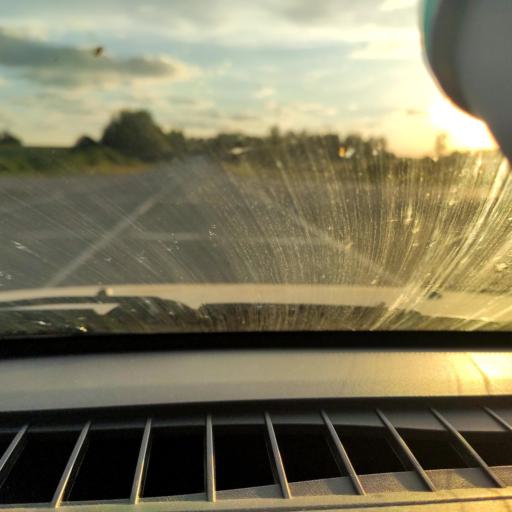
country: RU
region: Kirov
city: Kotel'nich
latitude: 58.3357
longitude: 48.3258
